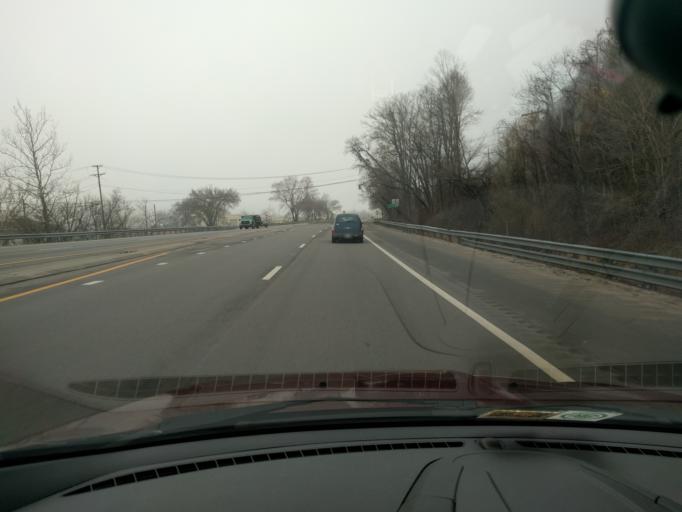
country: US
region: West Virginia
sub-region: Kanawha County
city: Chesapeake
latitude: 38.2141
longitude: -81.5157
